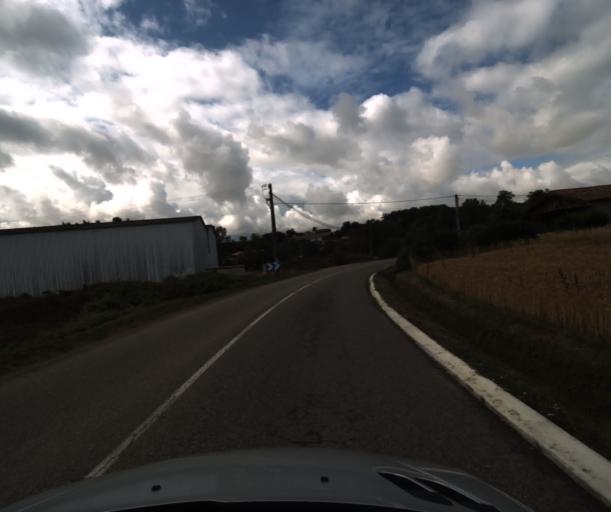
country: FR
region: Midi-Pyrenees
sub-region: Departement du Tarn-et-Garonne
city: Saint-Nicolas-de-la-Grave
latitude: 44.0188
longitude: 1.0040
